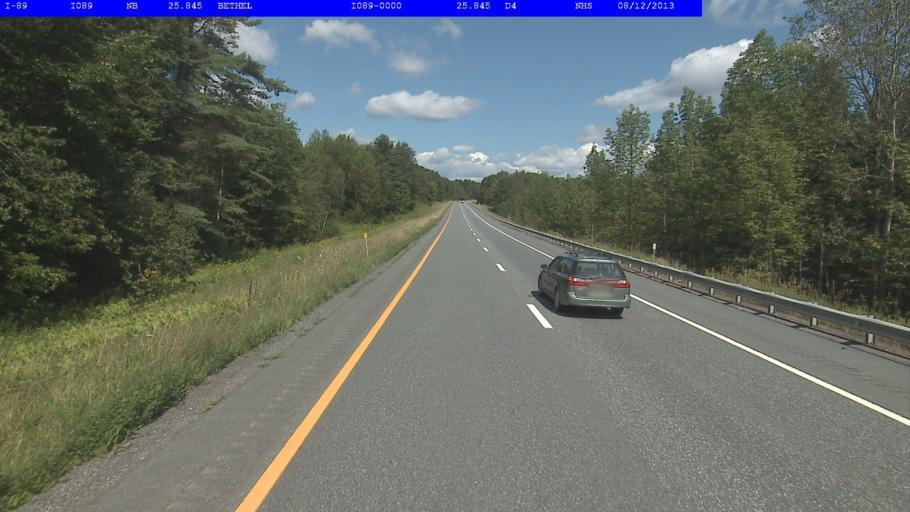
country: US
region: Vermont
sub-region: Orange County
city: Randolph
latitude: 43.8730
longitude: -72.6121
